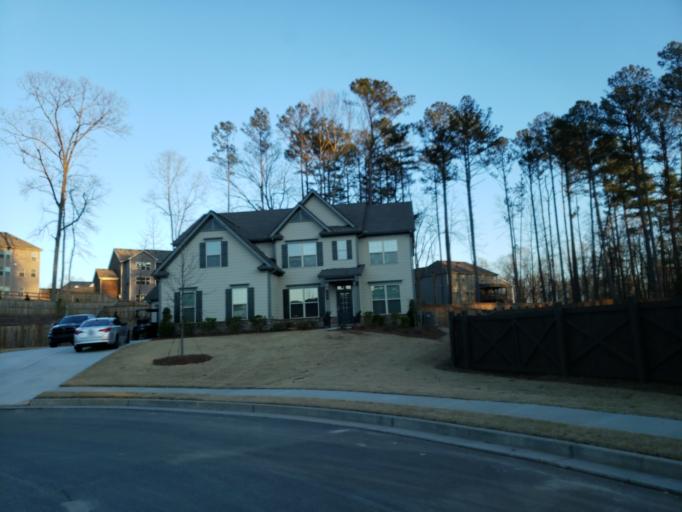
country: US
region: Georgia
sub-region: Cherokee County
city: Woodstock
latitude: 34.1157
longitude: -84.4544
